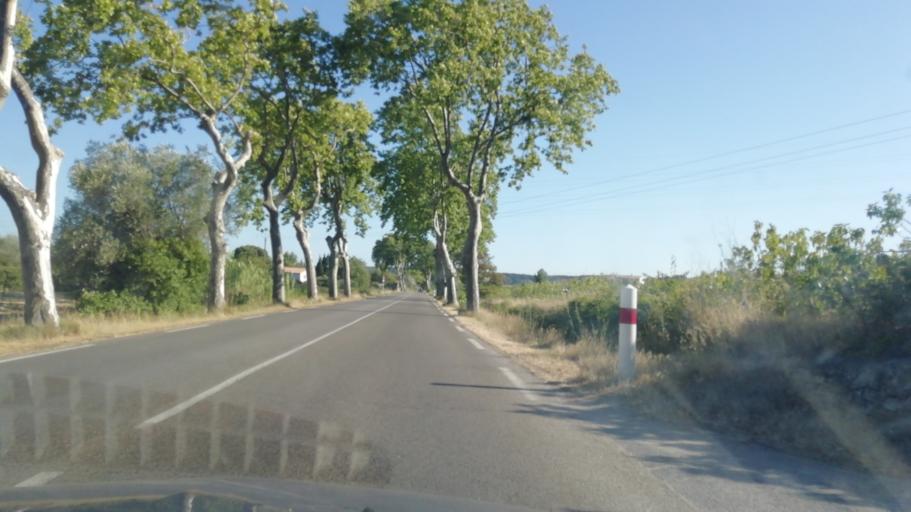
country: FR
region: Languedoc-Roussillon
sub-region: Departement de l'Herault
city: Nebian
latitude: 43.6139
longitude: 3.4368
